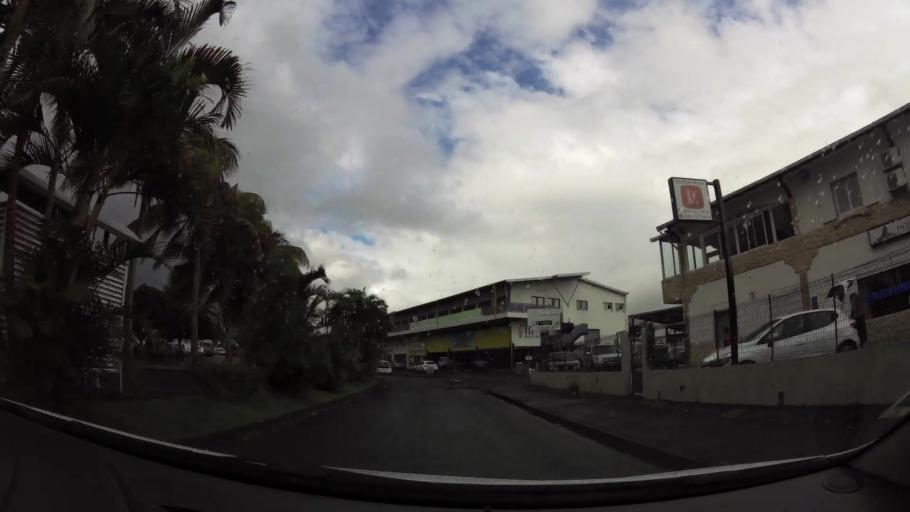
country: RE
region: Reunion
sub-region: Reunion
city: Saint-Andre
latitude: -20.9309
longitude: 55.6376
